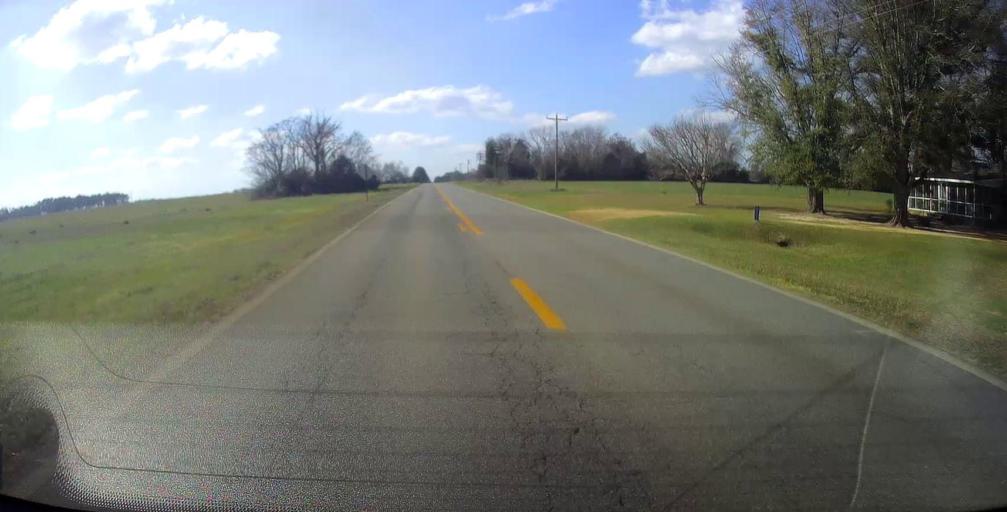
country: US
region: Georgia
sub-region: Laurens County
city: Dublin
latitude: 32.5632
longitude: -83.0179
